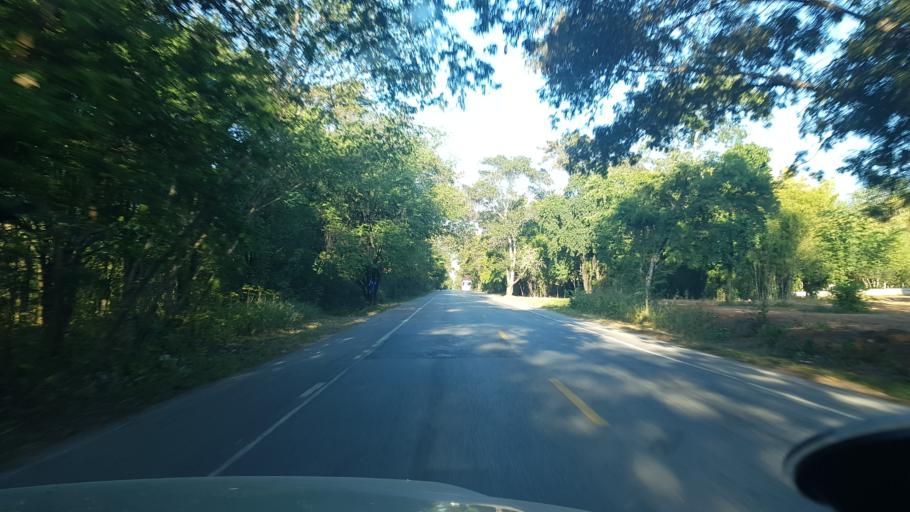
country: TH
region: Khon Kaen
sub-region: Amphoe Phu Pha Man
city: Phu Pha Man
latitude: 16.6225
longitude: 101.8613
